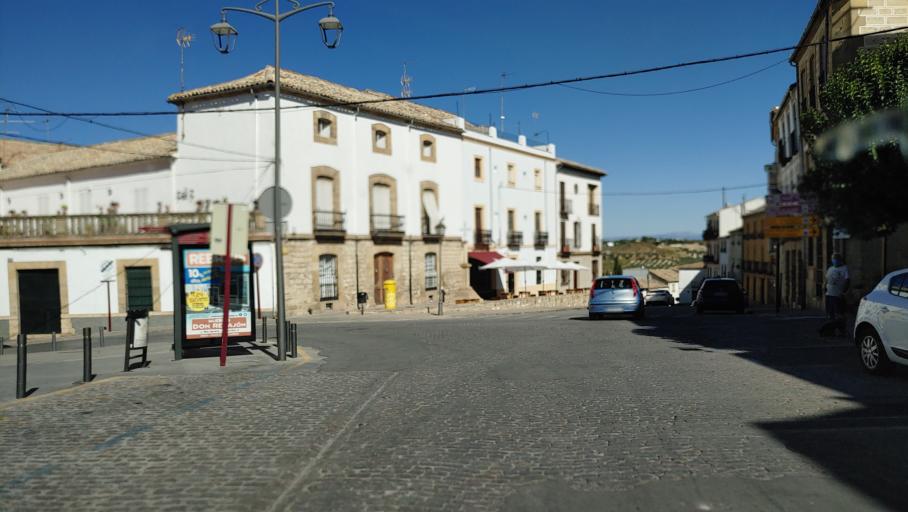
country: ES
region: Andalusia
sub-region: Provincia de Jaen
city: Ubeda
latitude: 38.0117
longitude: -3.3680
